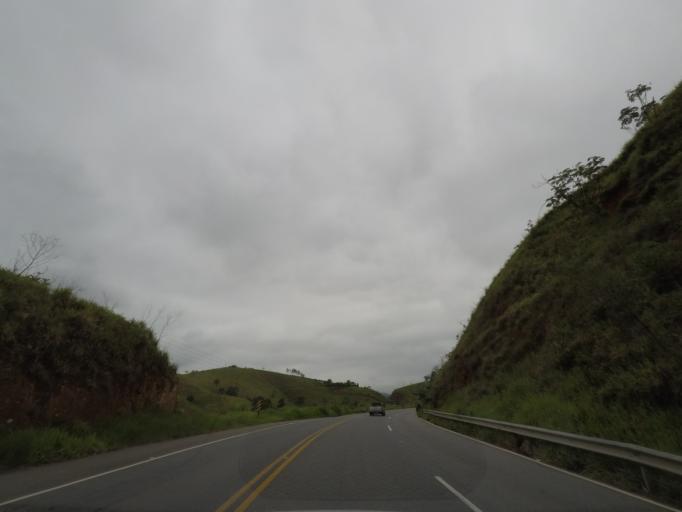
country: BR
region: Sao Paulo
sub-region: Guaratingueta
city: Guaratingueta
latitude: -22.8784
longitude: -45.1644
